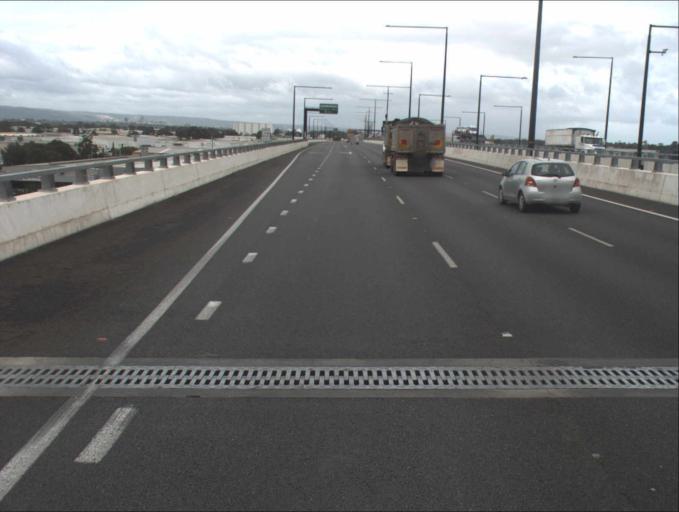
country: AU
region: South Australia
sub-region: Port Adelaide Enfield
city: Blair Athol
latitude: -34.8411
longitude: 138.5640
